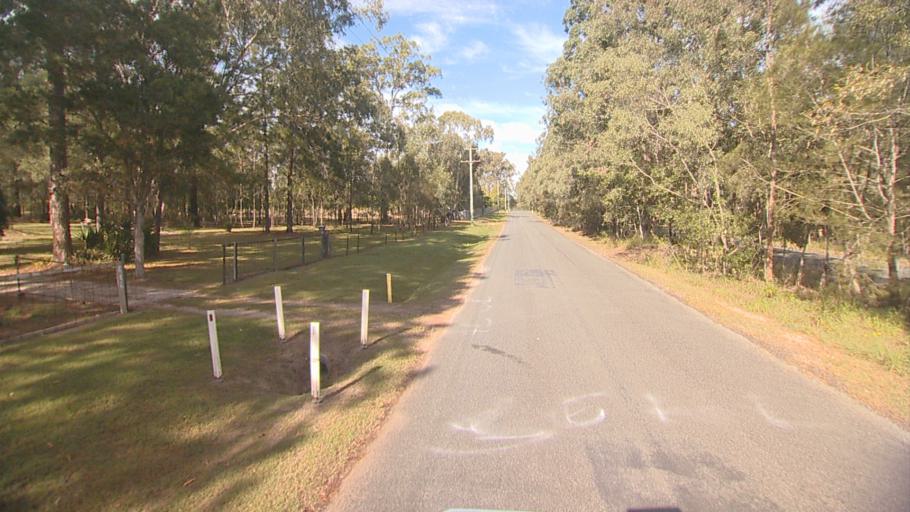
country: AU
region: Queensland
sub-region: Brisbane
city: Forest Lake
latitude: -27.6546
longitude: 152.9830
